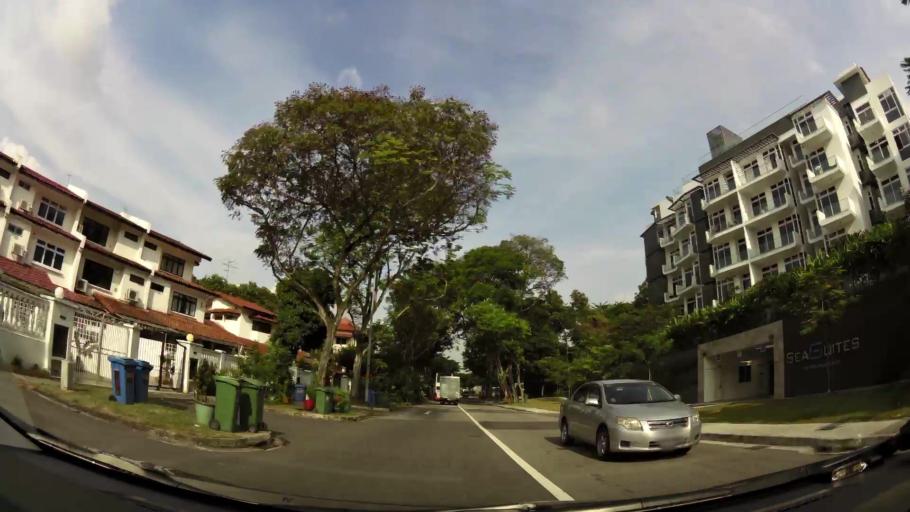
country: SG
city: Singapore
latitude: 1.2820
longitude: 103.7832
